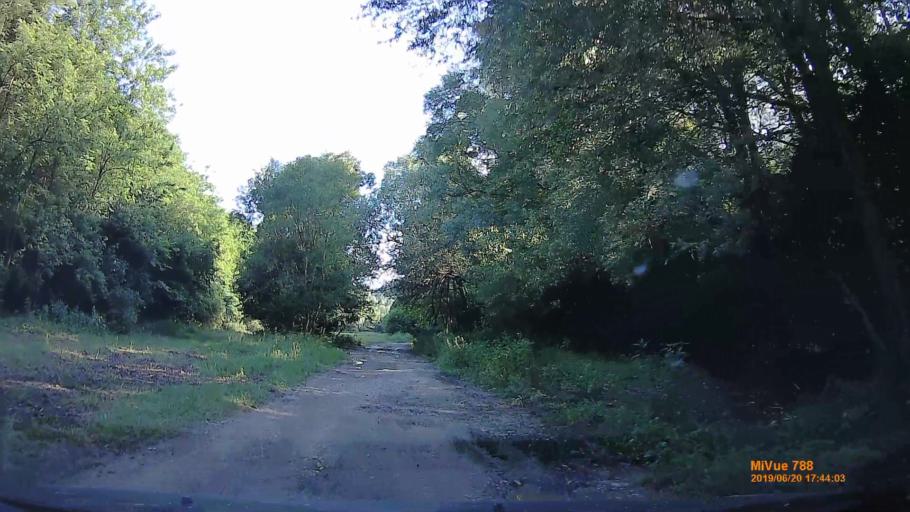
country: HU
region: Baranya
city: Buekkoesd
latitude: 46.1374
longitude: 18.0038
